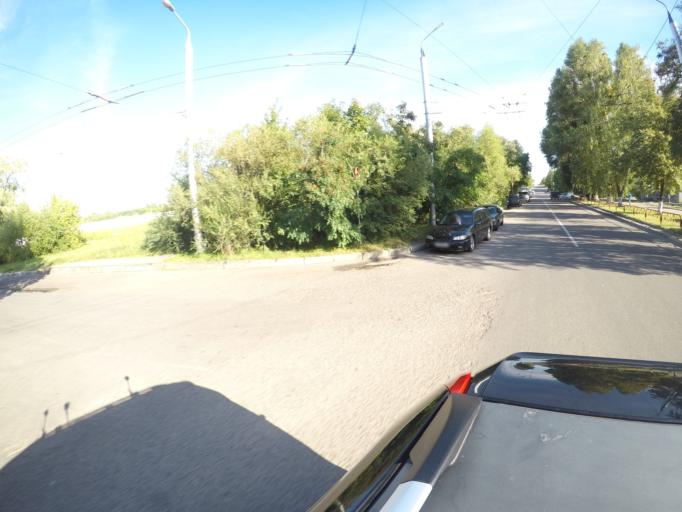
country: BY
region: Grodnenskaya
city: Hrodna
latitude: 53.7138
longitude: 23.8256
